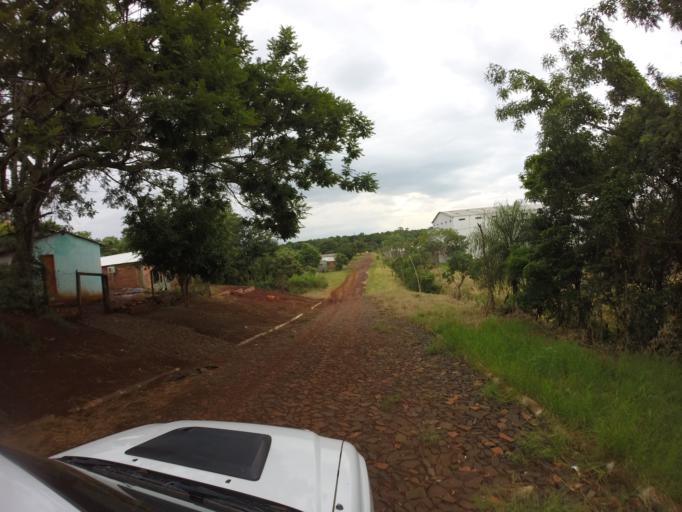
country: PY
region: Alto Parana
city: Ciudad del Este
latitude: -25.4126
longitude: -54.6525
